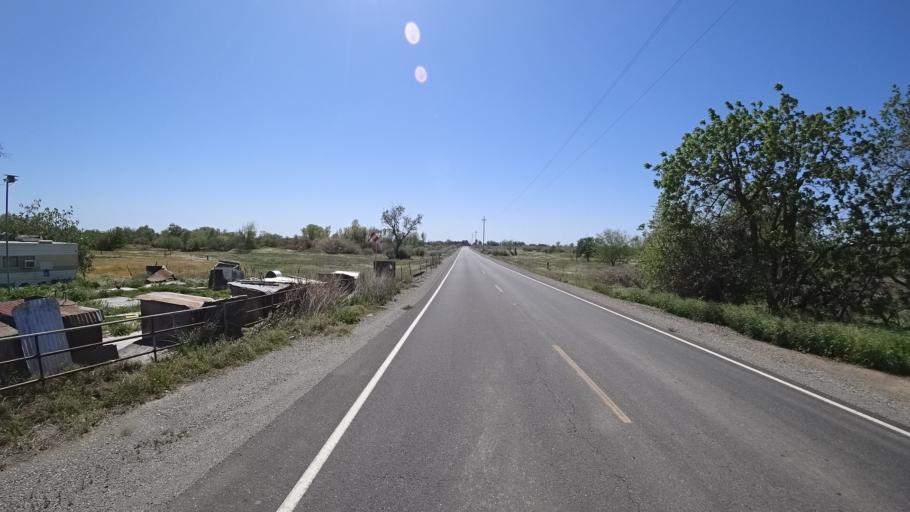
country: US
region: California
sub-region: Glenn County
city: Orland
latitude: 39.7646
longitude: -122.1409
